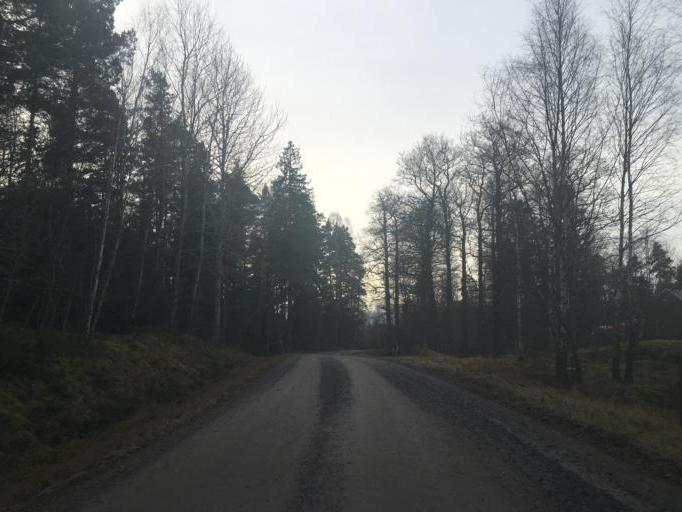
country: SE
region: OEstergoetland
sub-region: Norrkopings Kommun
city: Kimstad
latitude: 58.4204
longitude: 16.0456
